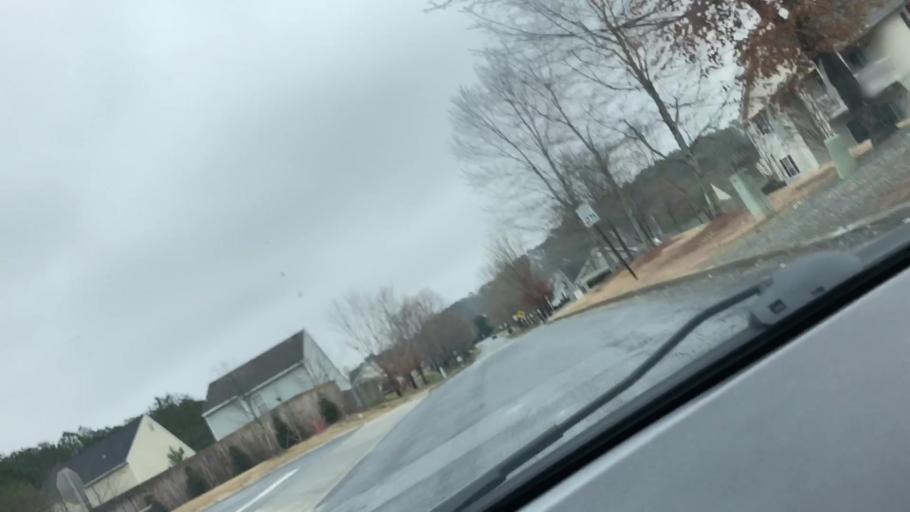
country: US
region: Georgia
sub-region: Bartow County
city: Cartersville
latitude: 34.2172
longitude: -84.8183
